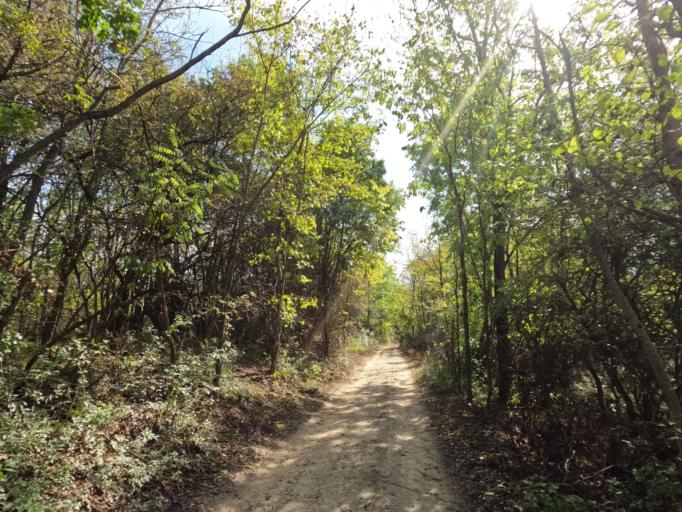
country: HU
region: Tolna
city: Szentgalpuszta
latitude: 46.3389
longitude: 18.6457
